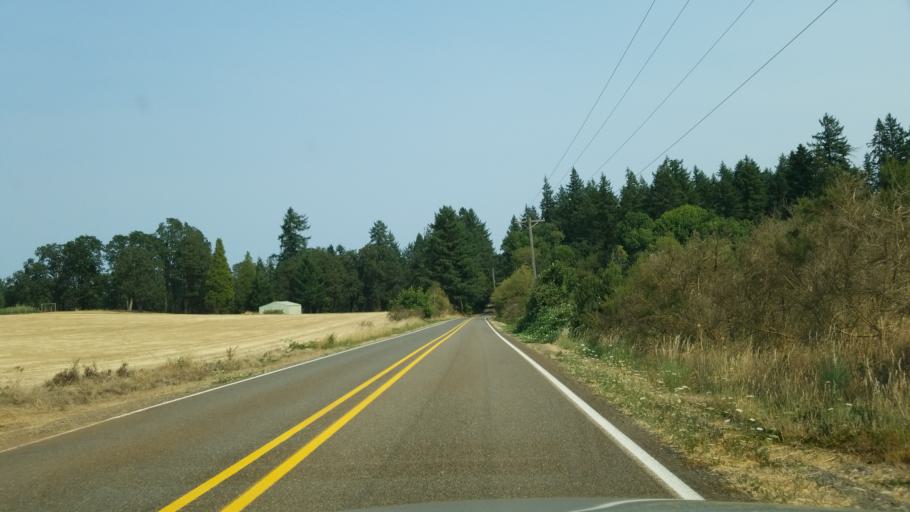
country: US
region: Oregon
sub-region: Marion County
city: Aumsville
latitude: 44.9181
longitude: -122.8373
